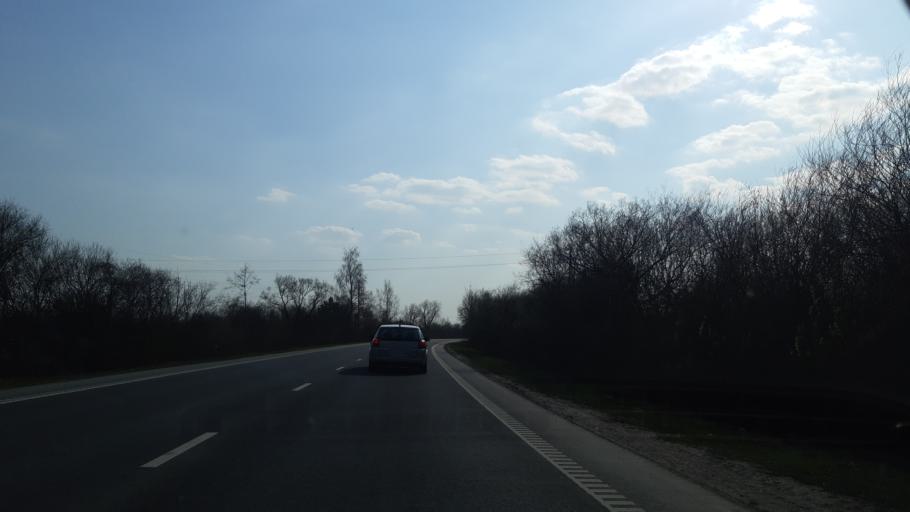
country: LT
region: Kauno apskritis
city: Dainava (Kaunas)
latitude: 54.8612
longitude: 23.9848
